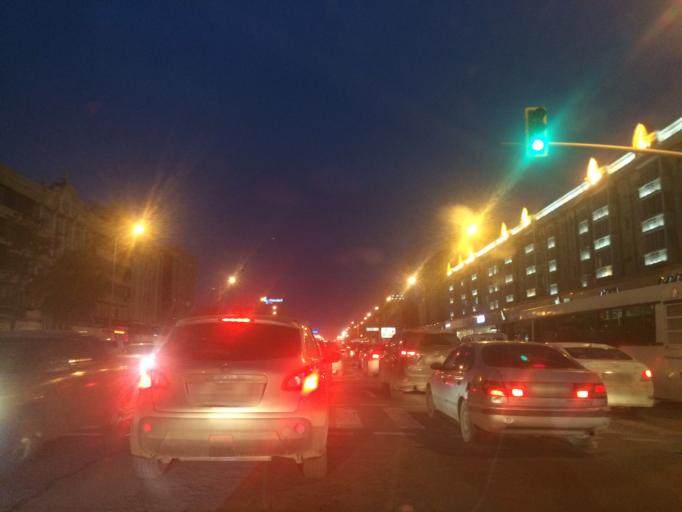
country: KZ
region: Astana Qalasy
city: Astana
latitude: 51.1607
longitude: 71.4288
